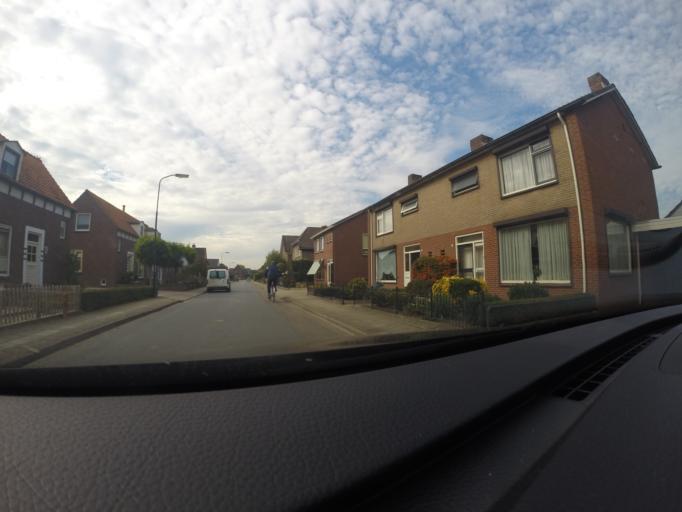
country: NL
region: Gelderland
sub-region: Gemeente Doetinchem
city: Doetinchem
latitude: 51.9624
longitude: 6.2144
